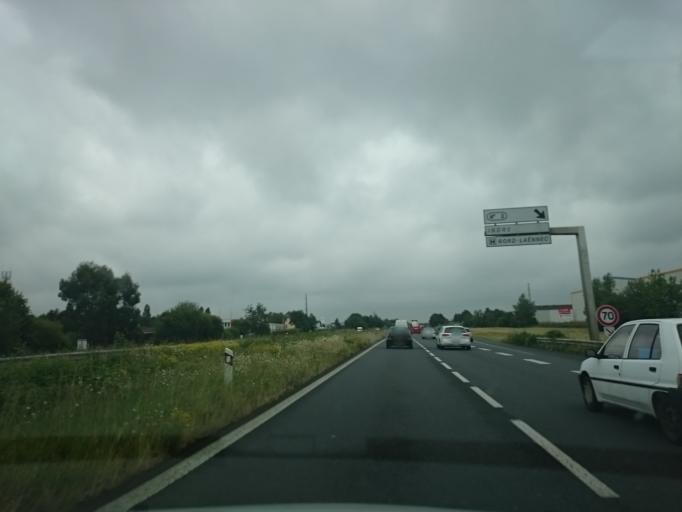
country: FR
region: Pays de la Loire
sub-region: Departement de la Loire-Atlantique
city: Saint-Herblain
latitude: 47.2354
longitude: -1.6540
